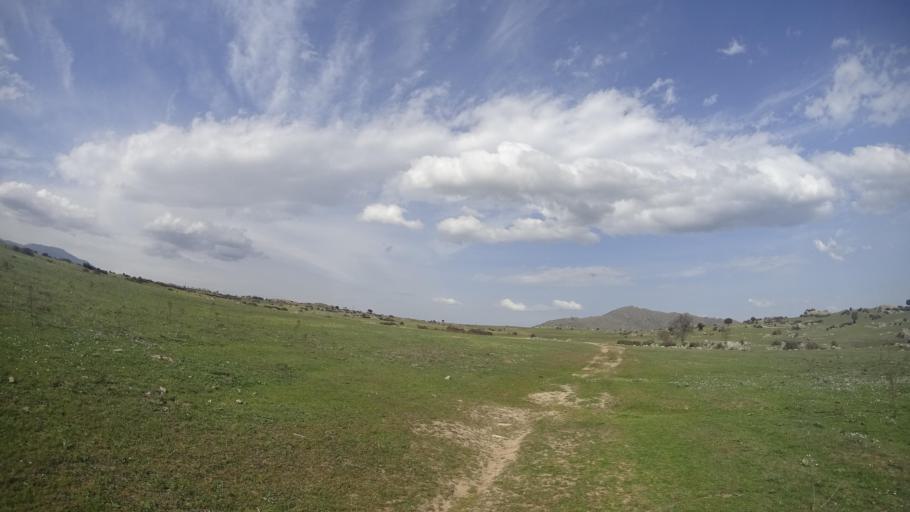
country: ES
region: Madrid
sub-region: Provincia de Madrid
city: Colmenar Viejo
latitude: 40.7052
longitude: -3.7554
